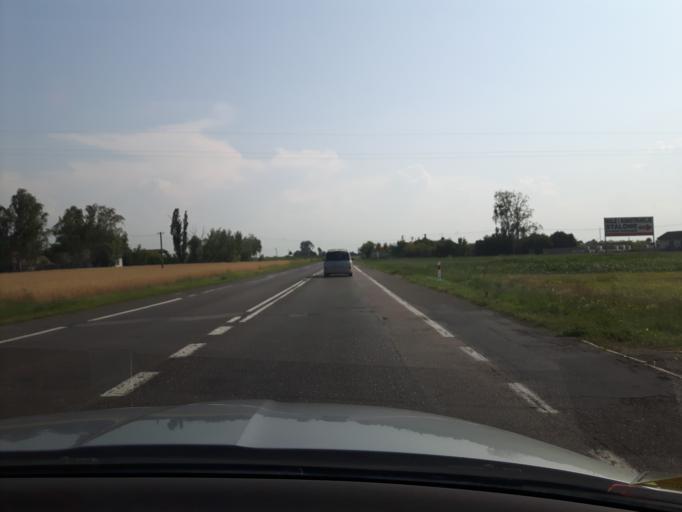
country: PL
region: Masovian Voivodeship
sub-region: Powiat plonski
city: Plonsk
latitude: 52.6562
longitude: 20.3792
